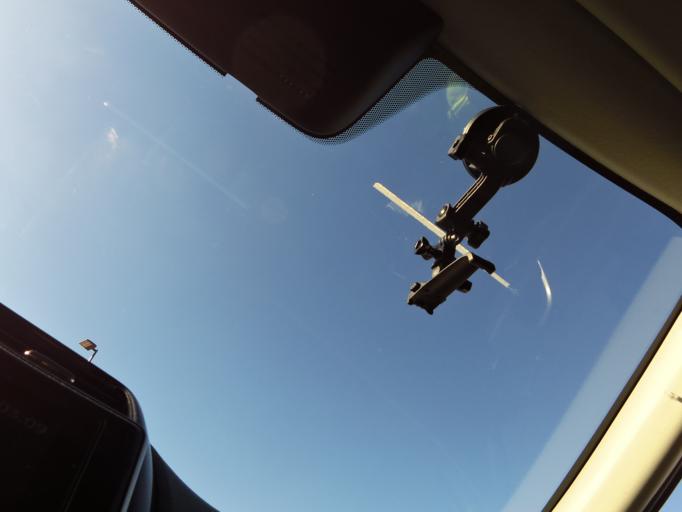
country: US
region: South Carolina
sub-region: Clarendon County
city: Manning
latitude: 33.5926
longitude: -80.3560
